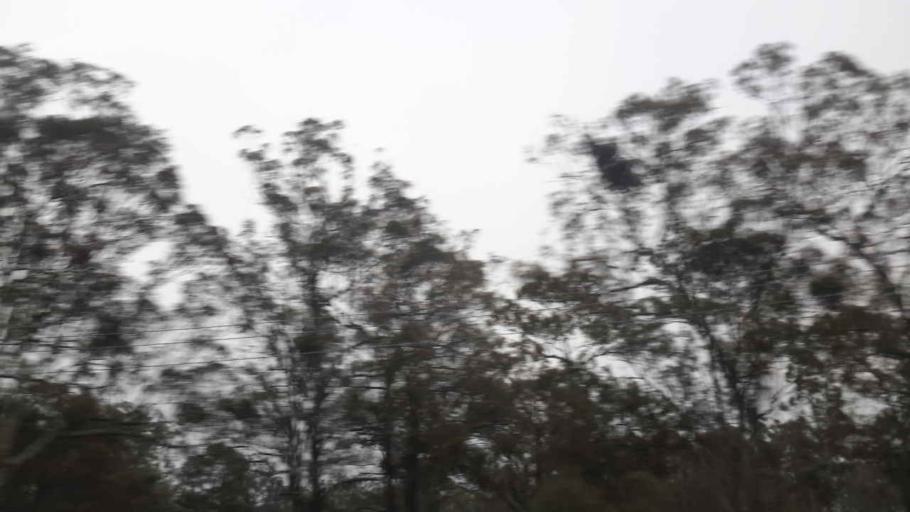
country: AU
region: New South Wales
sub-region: Camden
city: Camden South
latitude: -34.1109
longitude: 150.6963
